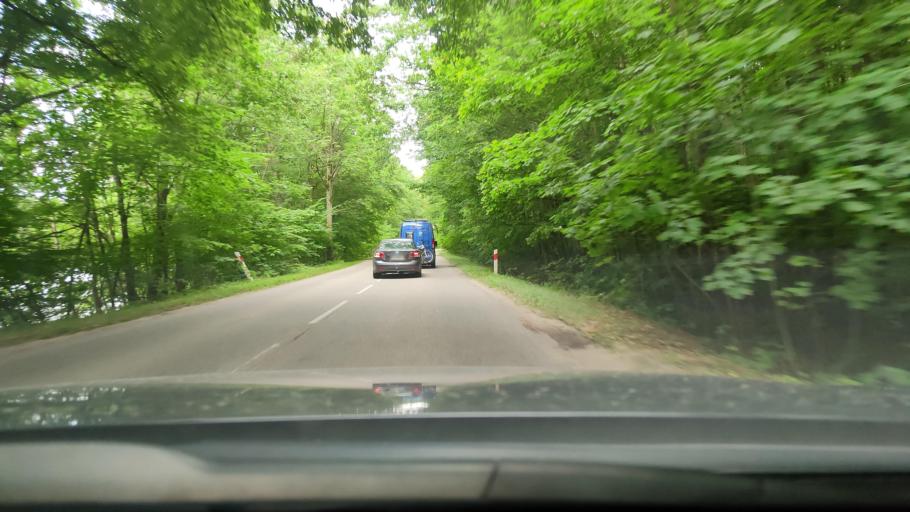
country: PL
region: Pomeranian Voivodeship
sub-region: Powiat pucki
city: Krokowa
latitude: 54.7135
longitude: 18.1652
